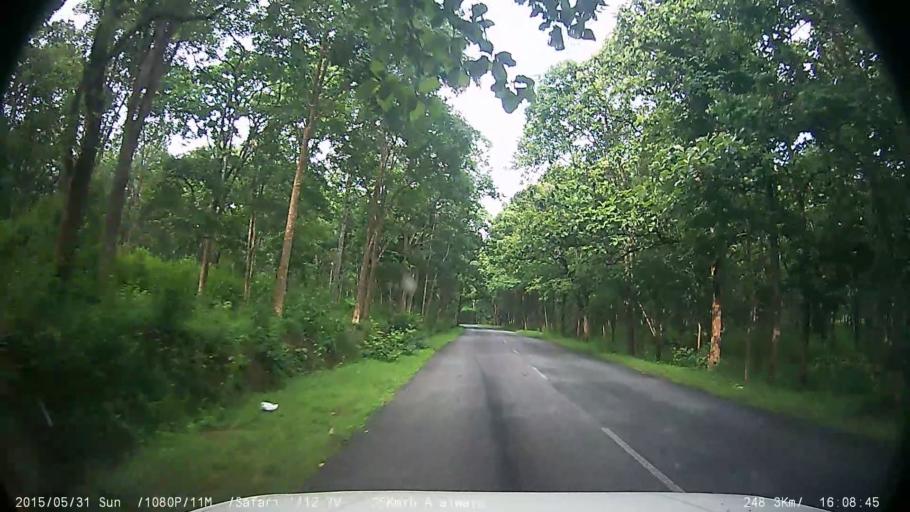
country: IN
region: Karnataka
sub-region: Mysore
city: Sargur
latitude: 11.7244
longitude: 76.4317
